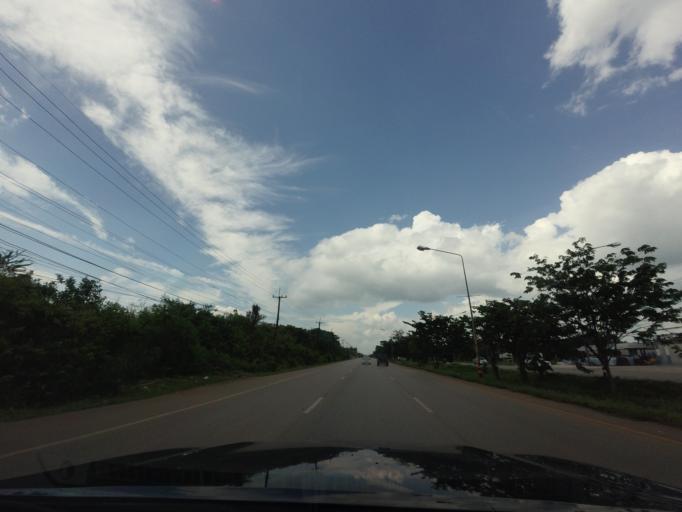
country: TH
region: Changwat Udon Thani
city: Udon Thani
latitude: 17.5373
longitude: 102.8000
